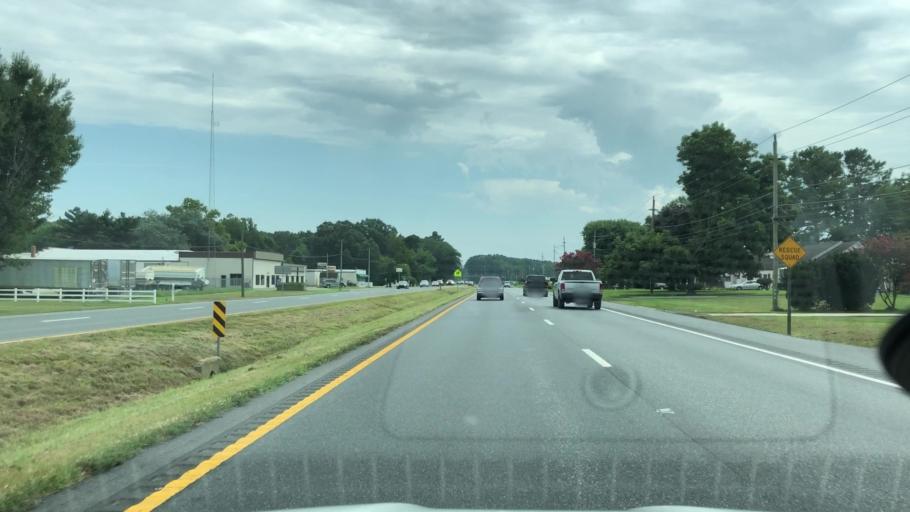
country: US
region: Virginia
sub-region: Accomack County
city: Wattsville
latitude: 37.9288
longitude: -75.5486
